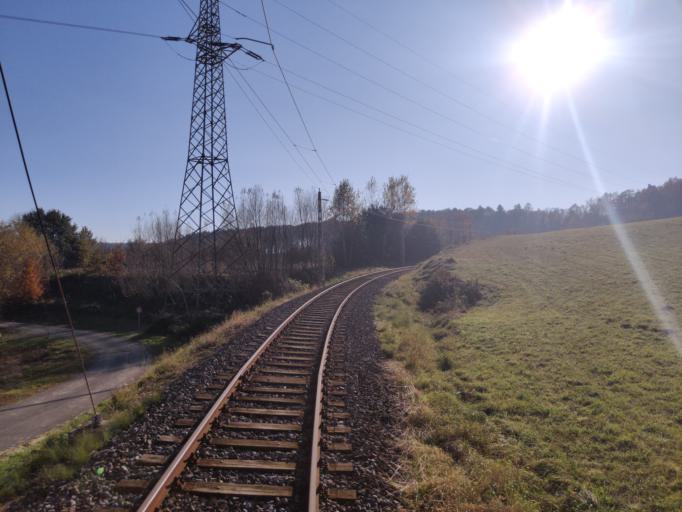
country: AT
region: Styria
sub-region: Politischer Bezirk Suedoststeiermark
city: Feldbach
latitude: 46.9320
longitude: 15.8557
